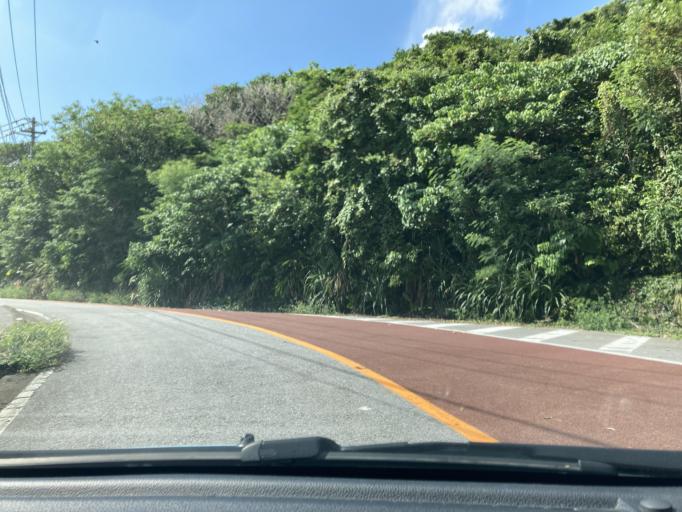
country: JP
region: Okinawa
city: Tomigusuku
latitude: 26.1449
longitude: 127.7941
